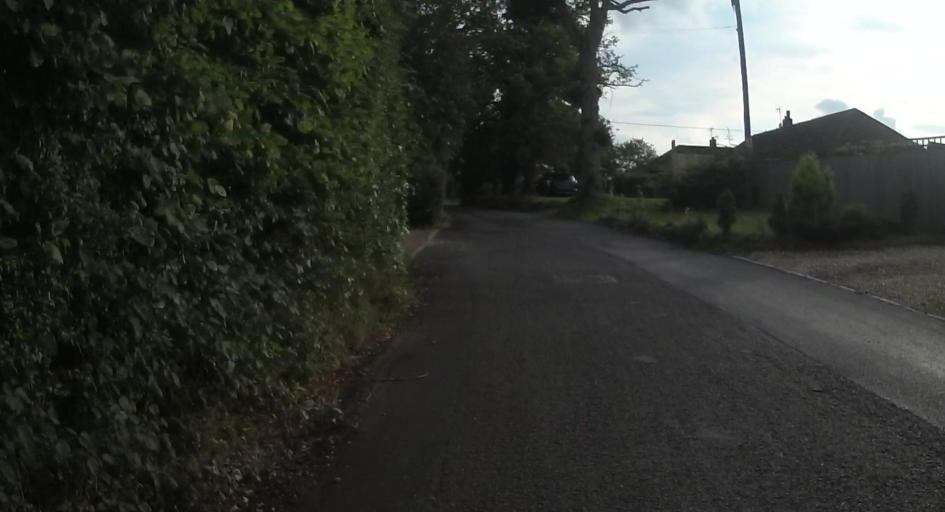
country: GB
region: England
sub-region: West Berkshire
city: Thatcham
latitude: 51.4168
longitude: -1.2239
